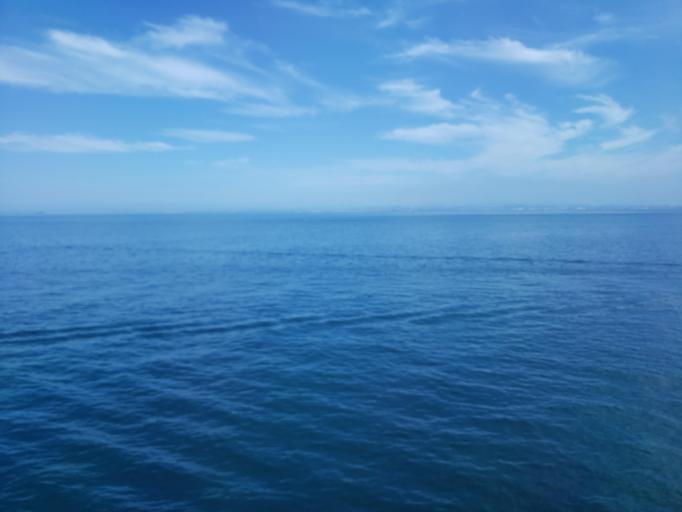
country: JP
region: Hyogo
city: Akashi
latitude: 34.5807
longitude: 134.8582
